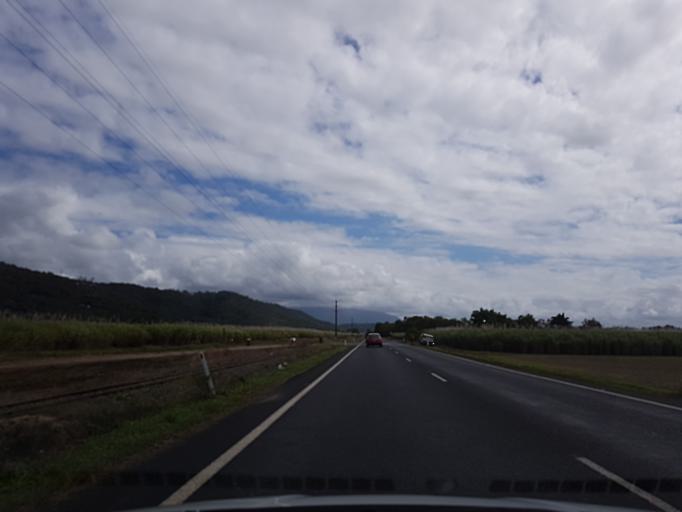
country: AU
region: Queensland
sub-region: Cairns
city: Port Douglas
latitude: -16.5028
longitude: 145.4348
